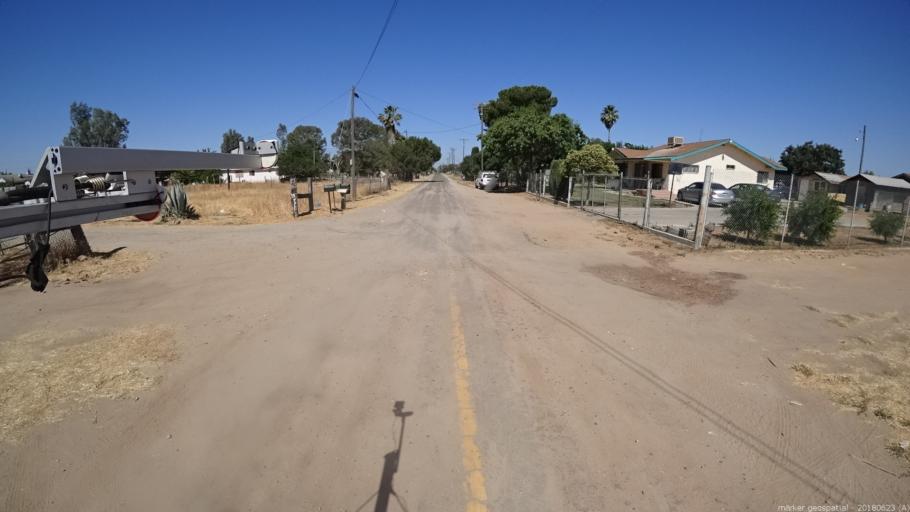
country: US
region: California
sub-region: Madera County
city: Parksdale
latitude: 36.9780
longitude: -120.0234
